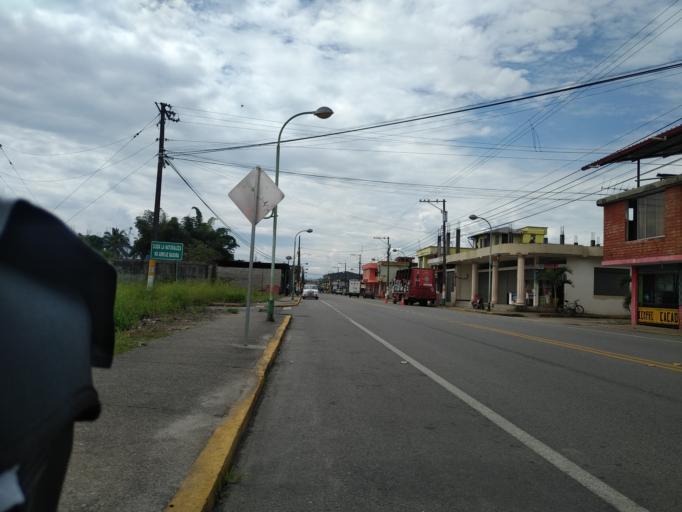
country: EC
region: Napo
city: Tena
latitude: -1.1707
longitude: -77.8561
